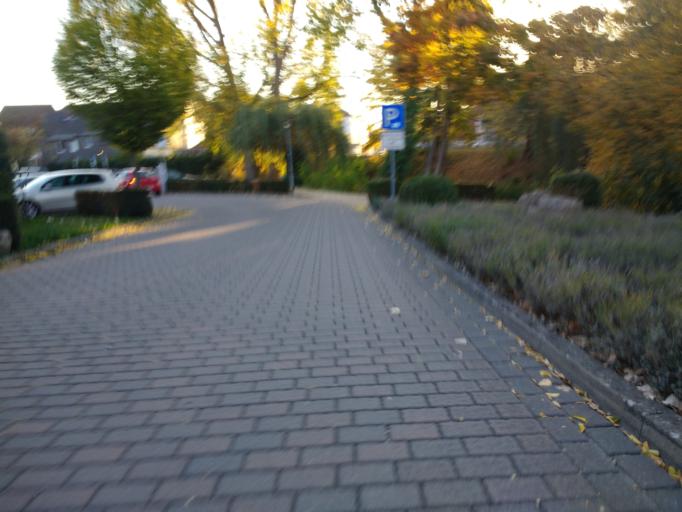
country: DE
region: Lower Saxony
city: Gifhorn
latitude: 52.4891
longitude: 10.5436
